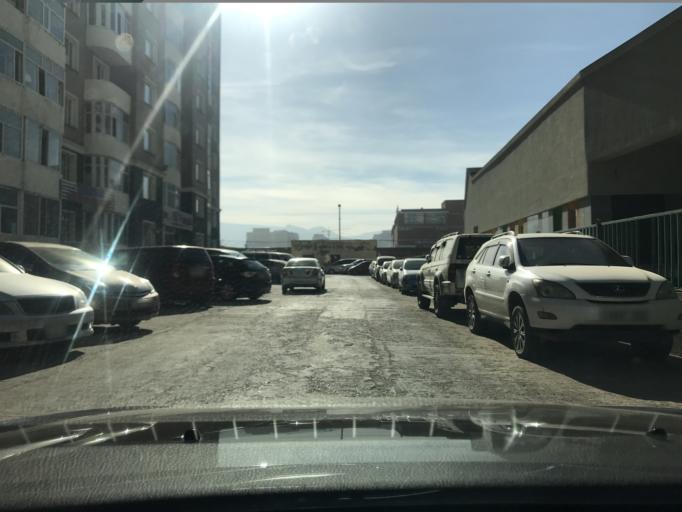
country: MN
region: Ulaanbaatar
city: Ulaanbaatar
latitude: 47.9120
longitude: 106.9464
